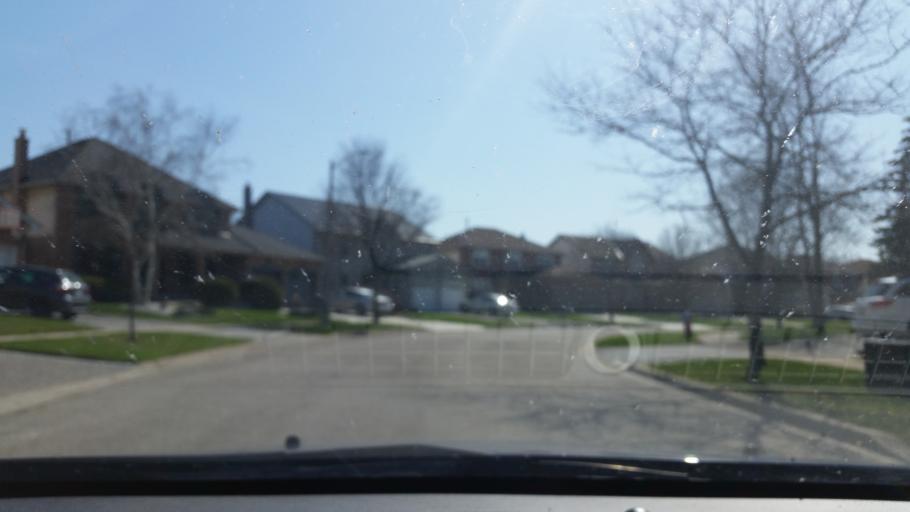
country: CA
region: Ontario
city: Burlington
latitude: 43.3807
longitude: -79.8240
